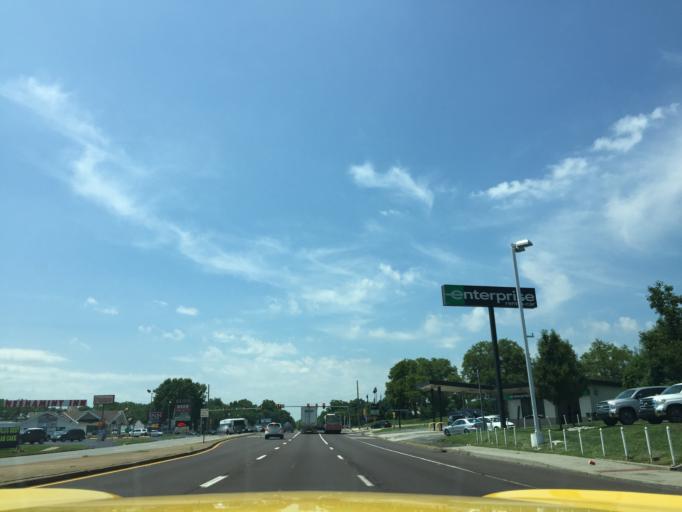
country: US
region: Pennsylvania
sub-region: Bucks County
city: Trevose
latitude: 40.1230
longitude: -74.9756
